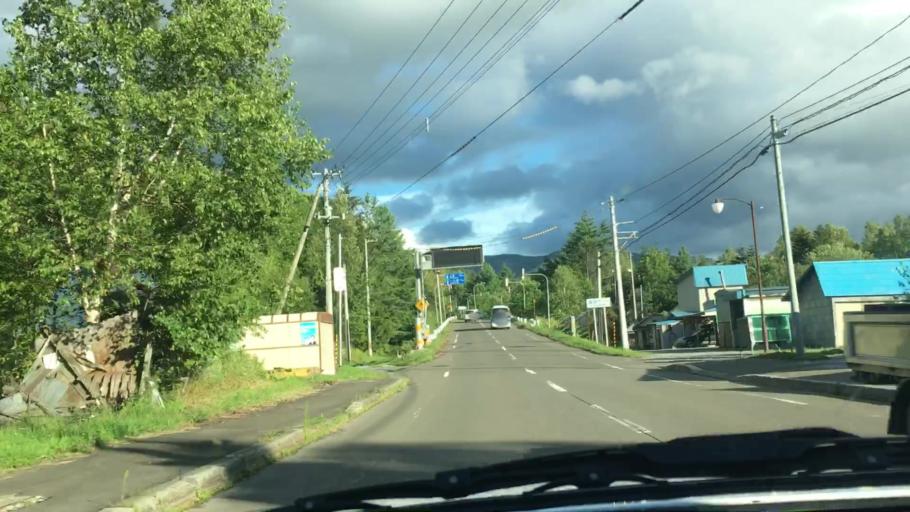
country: JP
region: Hokkaido
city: Shimo-furano
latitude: 43.1235
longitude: 142.6781
